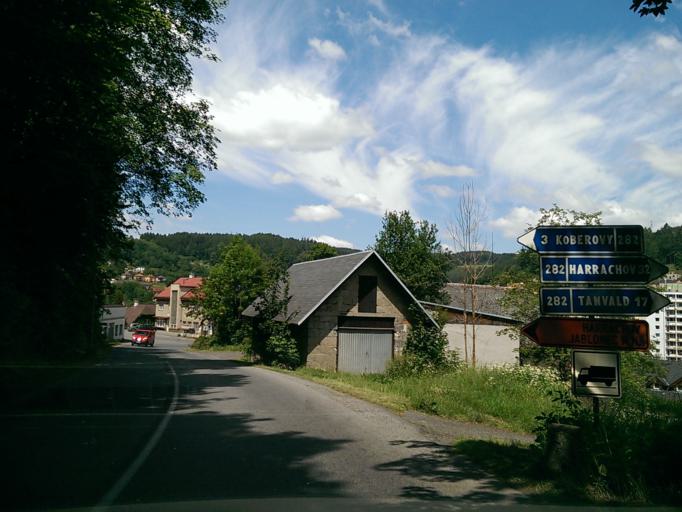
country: CZ
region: Liberecky
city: Zelezny Brod
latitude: 50.6384
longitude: 15.2608
